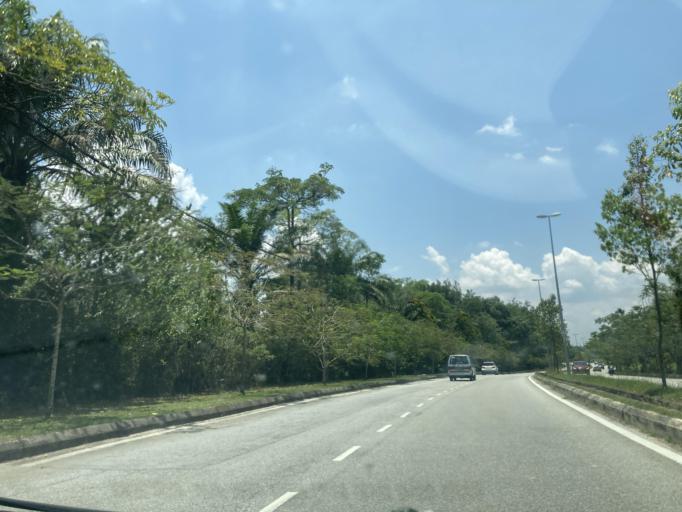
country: MY
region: Selangor
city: Batu Arang
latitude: 3.2956
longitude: 101.4860
